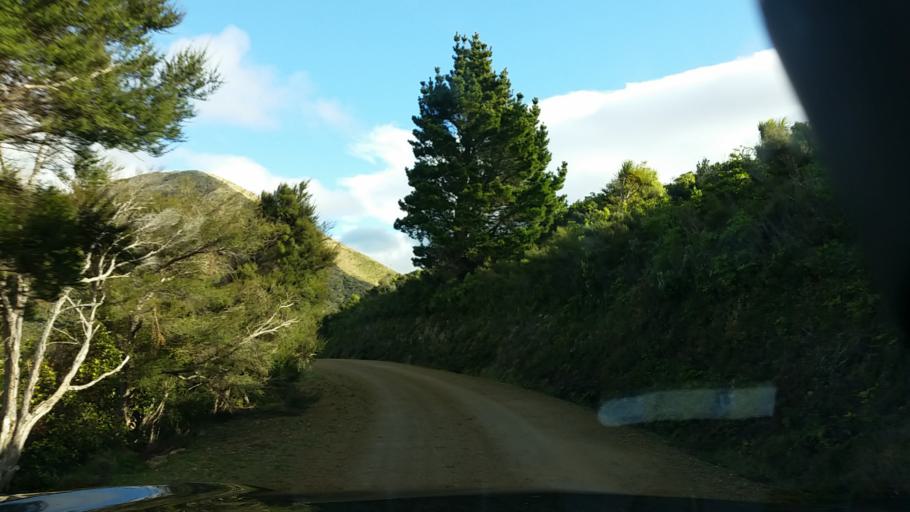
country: NZ
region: Marlborough
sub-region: Marlborough District
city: Picton
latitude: -40.9657
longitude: 173.8993
